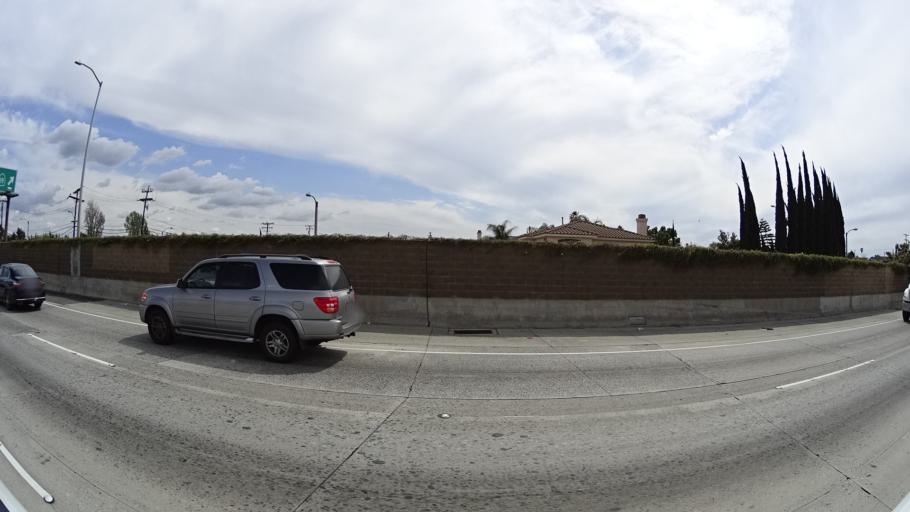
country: US
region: California
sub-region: Los Angeles County
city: Rosemead
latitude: 34.0720
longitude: -118.0763
